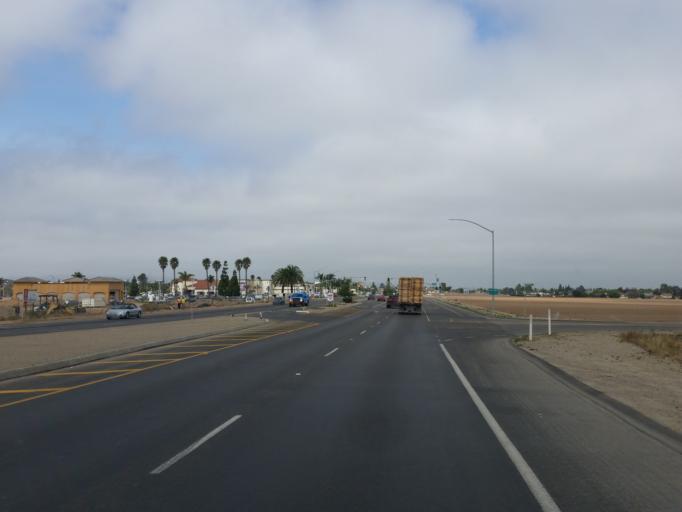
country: US
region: California
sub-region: Santa Barbara County
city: Santa Maria
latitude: 34.9237
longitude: -120.4192
